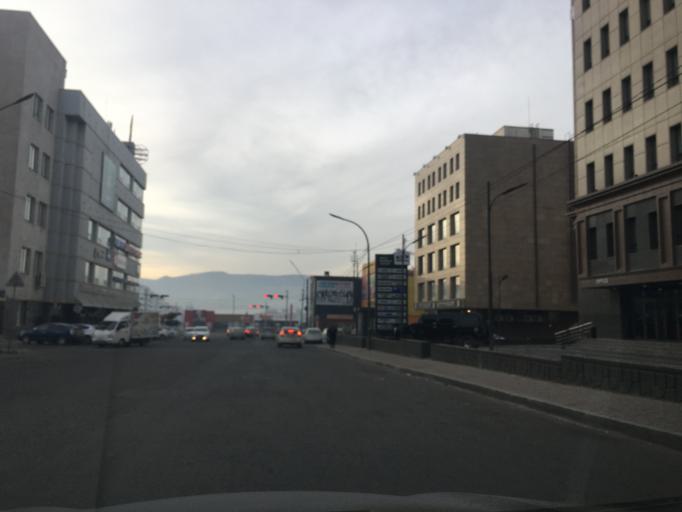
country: MN
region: Ulaanbaatar
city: Ulaanbaatar
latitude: 47.9240
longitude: 106.8758
